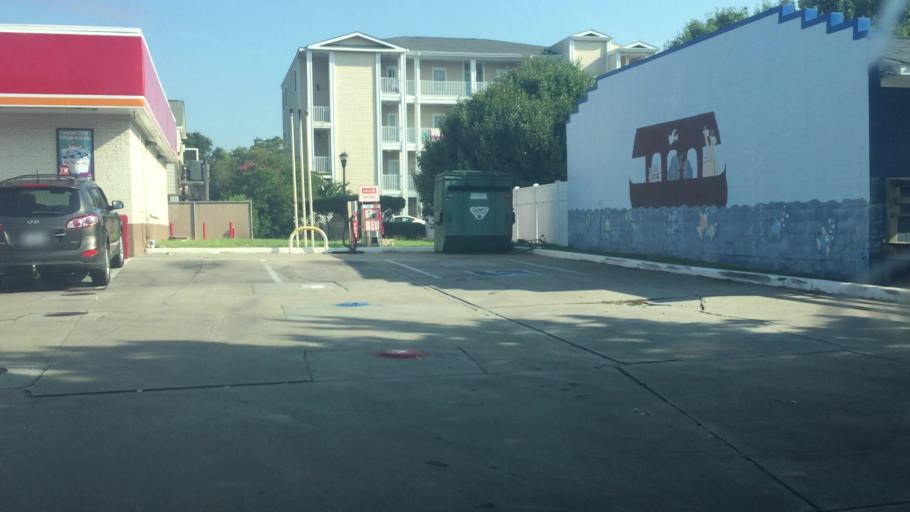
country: US
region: South Carolina
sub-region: Horry County
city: North Myrtle Beach
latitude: 33.8310
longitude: -78.6437
